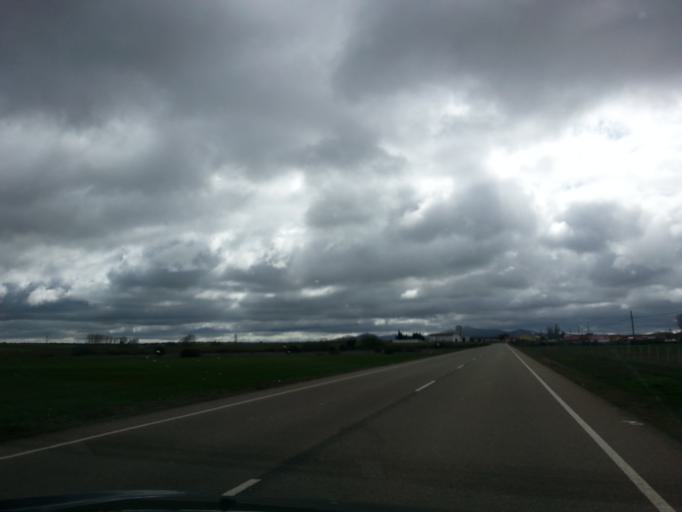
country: ES
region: Castille and Leon
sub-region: Provincia de Salamanca
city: Abusejo
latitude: 40.7162
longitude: -6.1464
